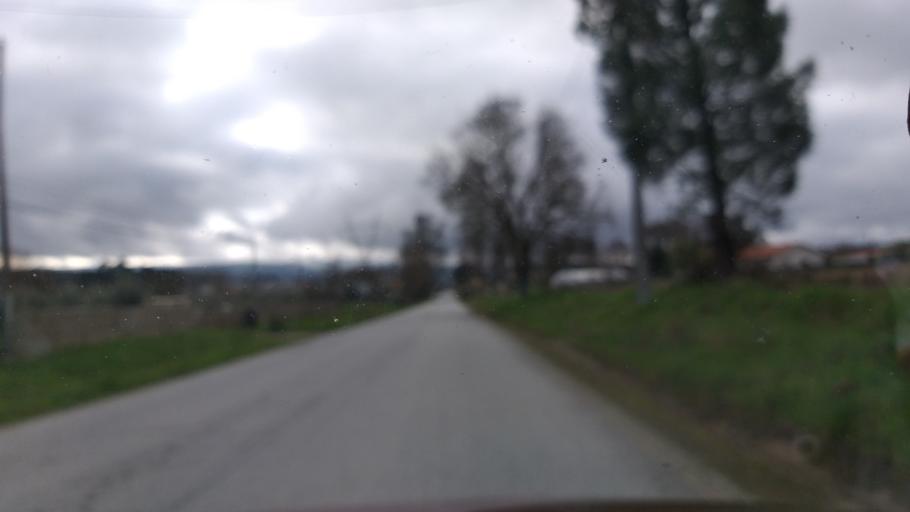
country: PT
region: Guarda
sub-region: Celorico da Beira
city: Celorico da Beira
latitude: 40.6745
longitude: -7.3797
